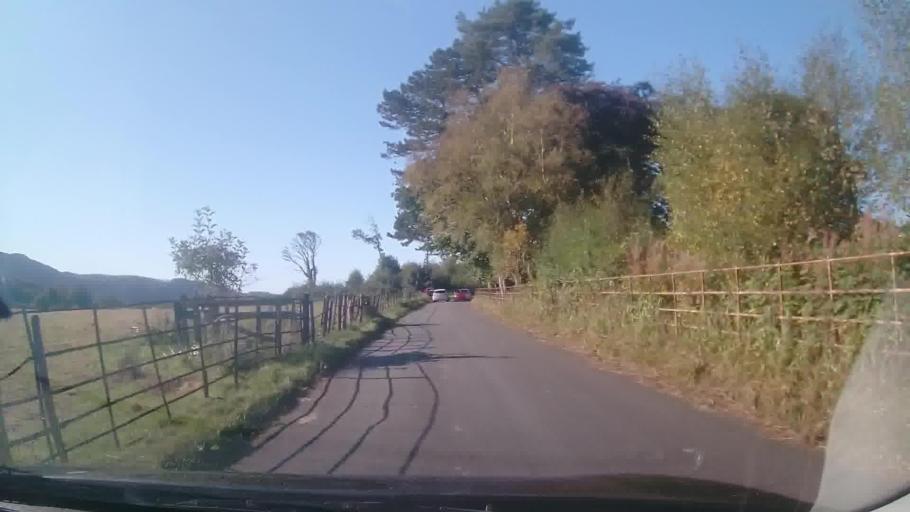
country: GB
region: England
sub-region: Cumbria
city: Seascale
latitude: 54.3899
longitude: -3.3781
